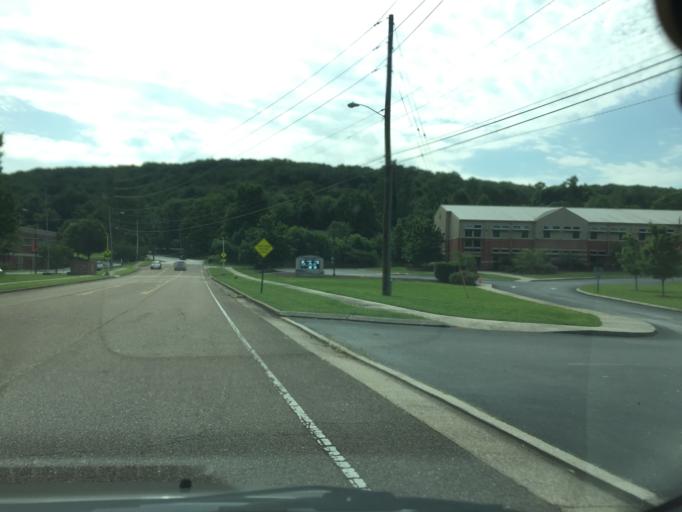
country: US
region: Tennessee
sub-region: Hamilton County
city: Collegedale
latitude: 35.0437
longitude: -85.0479
